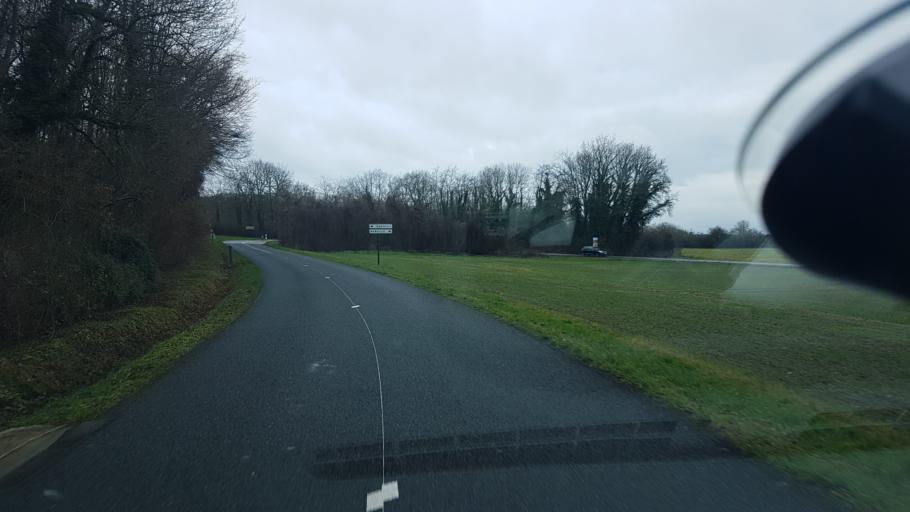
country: FR
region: Ile-de-France
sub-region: Departement de Seine-et-Marne
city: Montigny-sur-Loing
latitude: 48.2767
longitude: 2.7601
